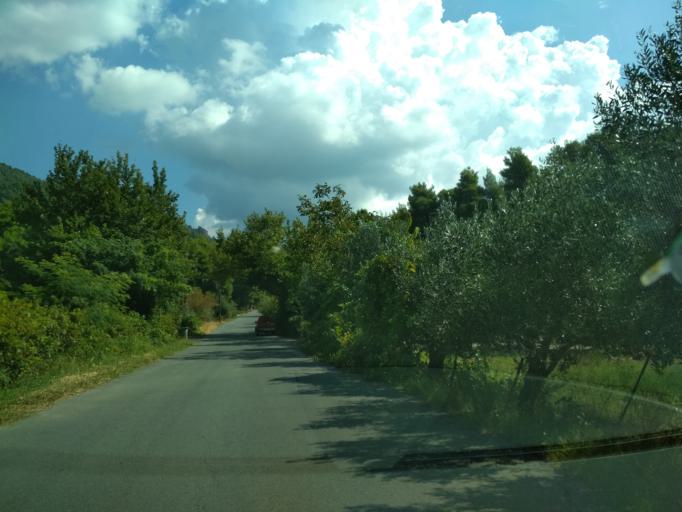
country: GR
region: Central Greece
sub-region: Nomos Evvoias
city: Roviai
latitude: 38.8262
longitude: 23.2582
